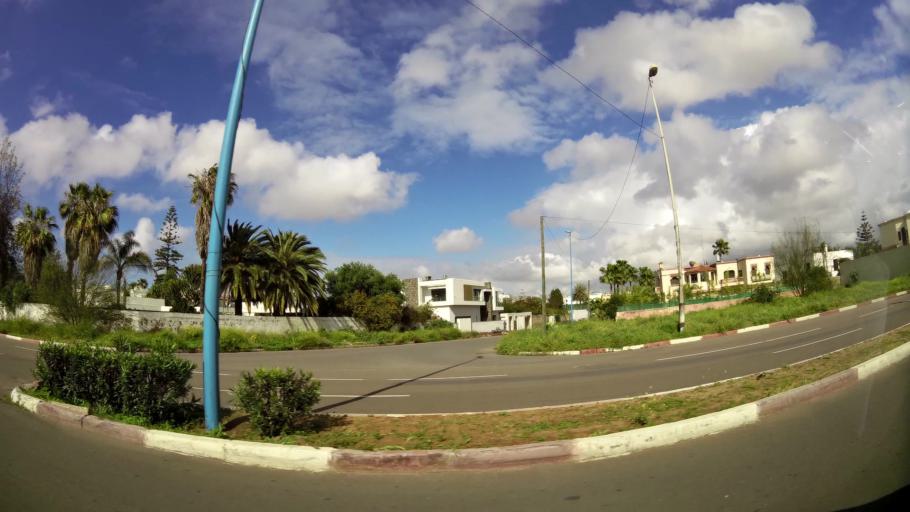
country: MA
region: Grand Casablanca
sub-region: Casablanca
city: Casablanca
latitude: 33.5445
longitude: -7.6207
